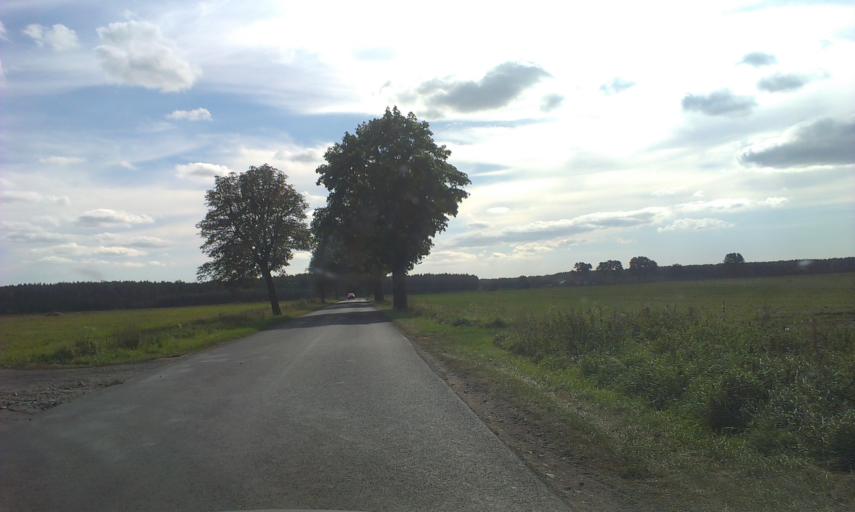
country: PL
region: Greater Poland Voivodeship
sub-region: Powiat zlotowski
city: Zlotow
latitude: 53.3263
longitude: 17.0890
